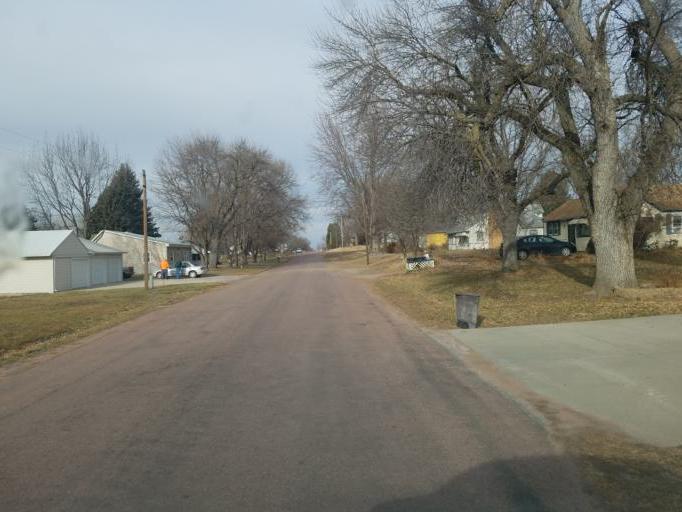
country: US
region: Nebraska
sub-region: Knox County
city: Creighton
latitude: 42.4622
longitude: -97.9091
